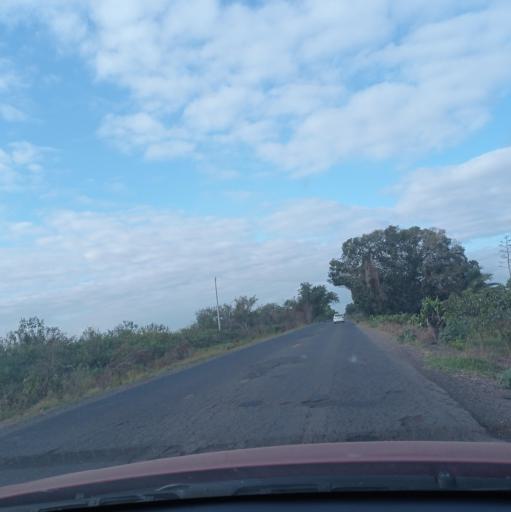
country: MX
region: Sinaloa
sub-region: Guasave
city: Las Quemazones
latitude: 25.6563
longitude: -108.5245
